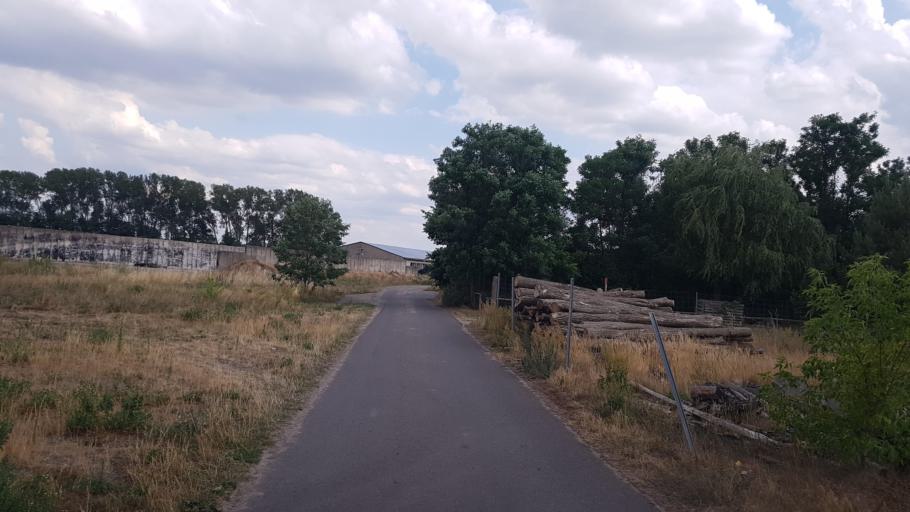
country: DE
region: Brandenburg
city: Golzow
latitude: 52.2371
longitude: 12.5850
